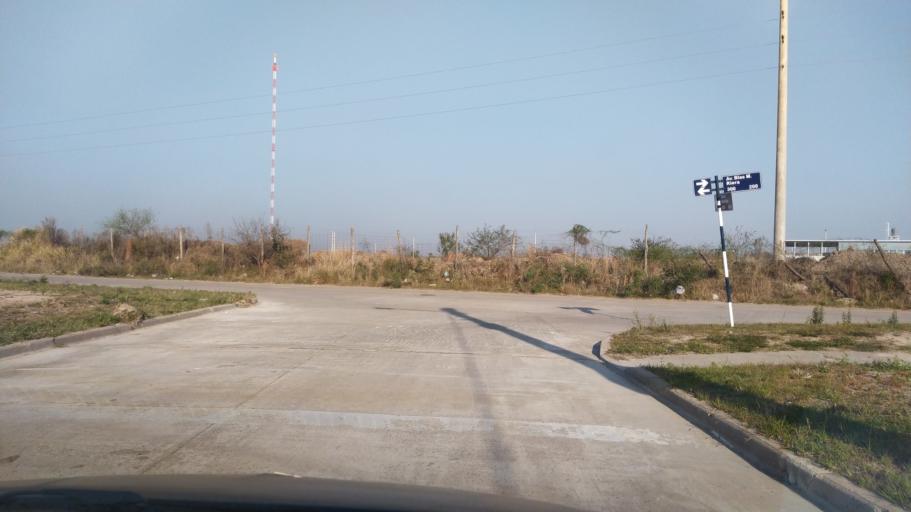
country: AR
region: Corrientes
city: Corrientes
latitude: -27.5268
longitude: -58.8079
